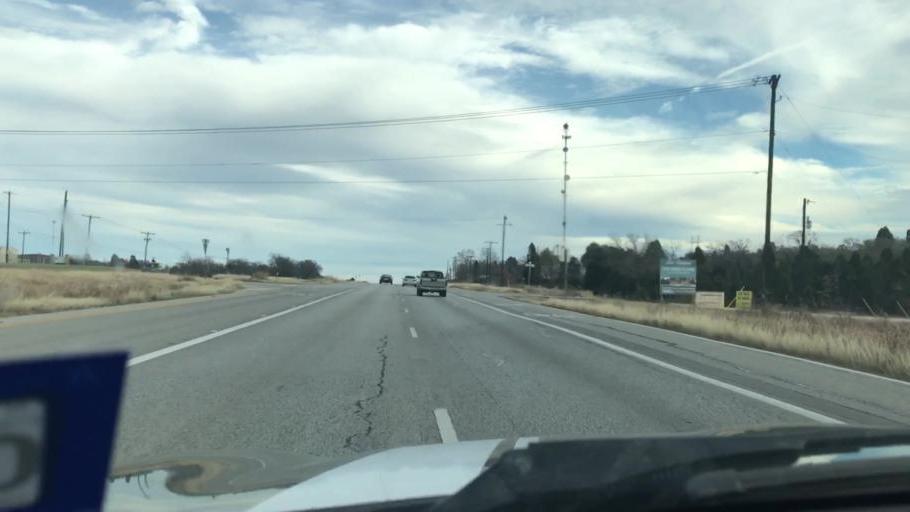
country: US
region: Texas
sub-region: Bastrop County
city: Elgin
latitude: 30.3289
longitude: -97.3410
